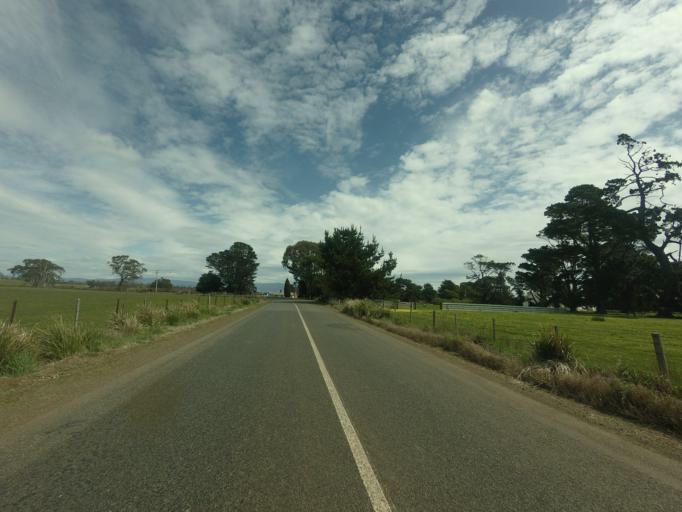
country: AU
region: Tasmania
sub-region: Northern Midlands
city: Longford
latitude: -41.7167
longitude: 147.1876
